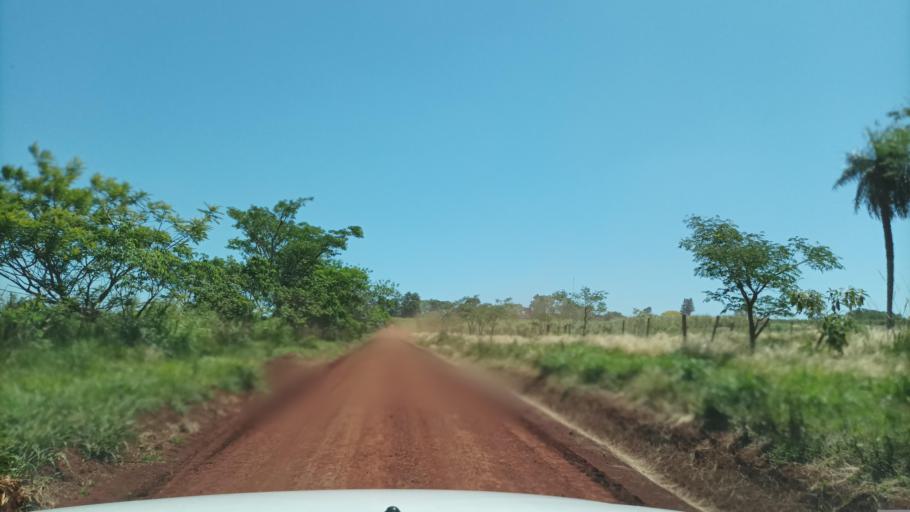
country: AR
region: Misiones
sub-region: Departamento de Apostoles
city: San Jose
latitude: -27.7897
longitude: -55.7107
